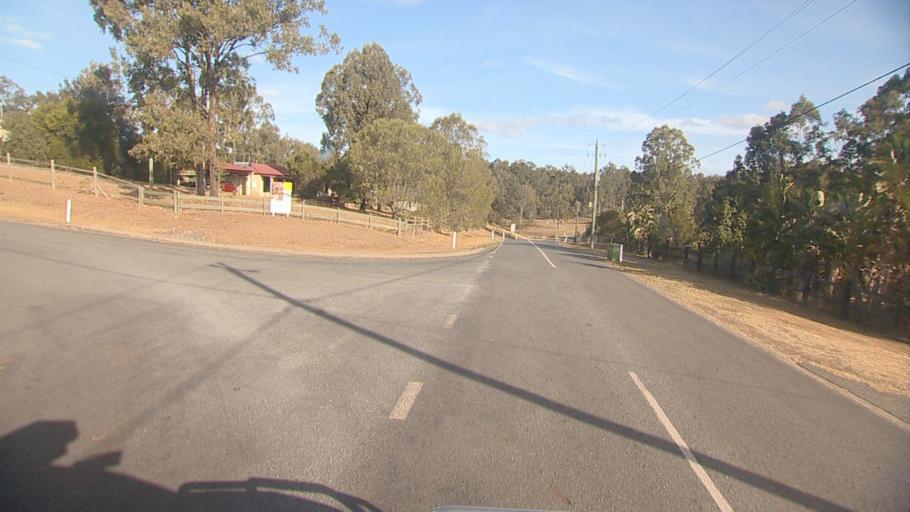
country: AU
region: Queensland
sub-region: Logan
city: Cedar Vale
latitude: -27.8754
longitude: 153.0027
